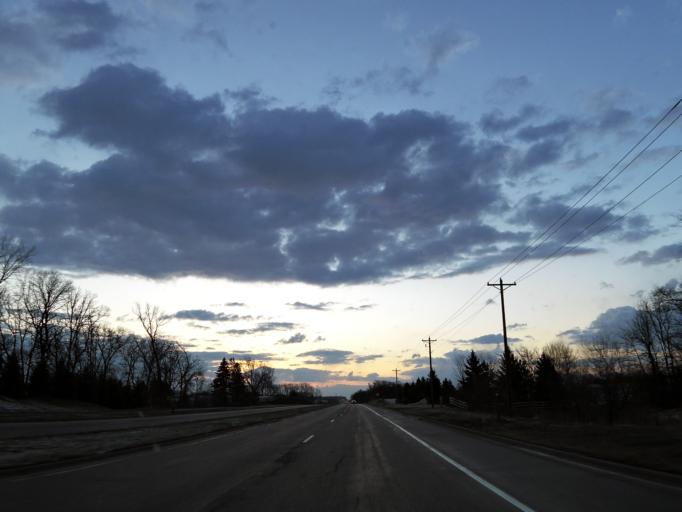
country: US
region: Minnesota
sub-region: Dakota County
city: Lakeville
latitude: 44.6812
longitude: -93.3144
